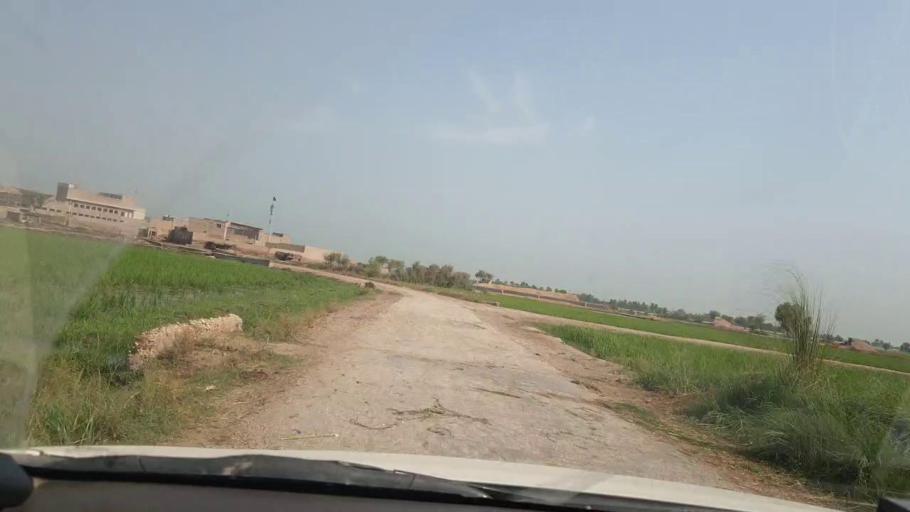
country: PK
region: Sindh
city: Chak
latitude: 27.8370
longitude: 68.7985
